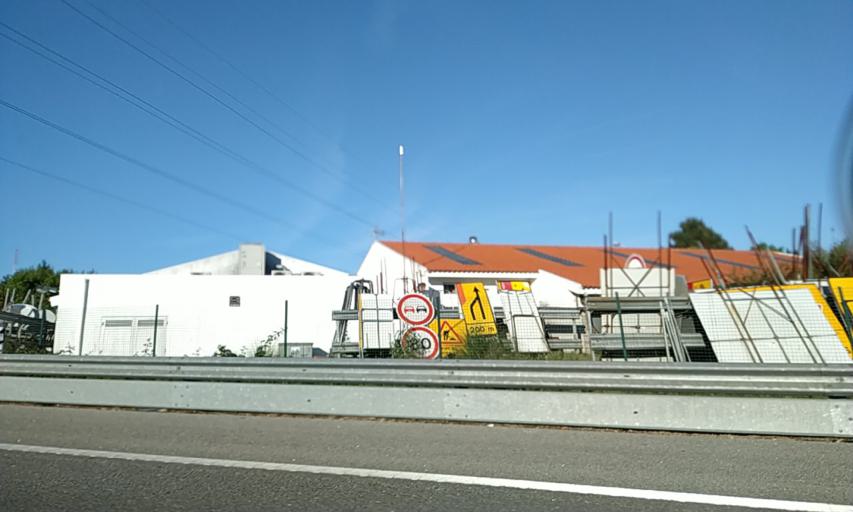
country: PT
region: Porto
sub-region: Valongo
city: Ermesinde
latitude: 41.2379
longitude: -8.5643
